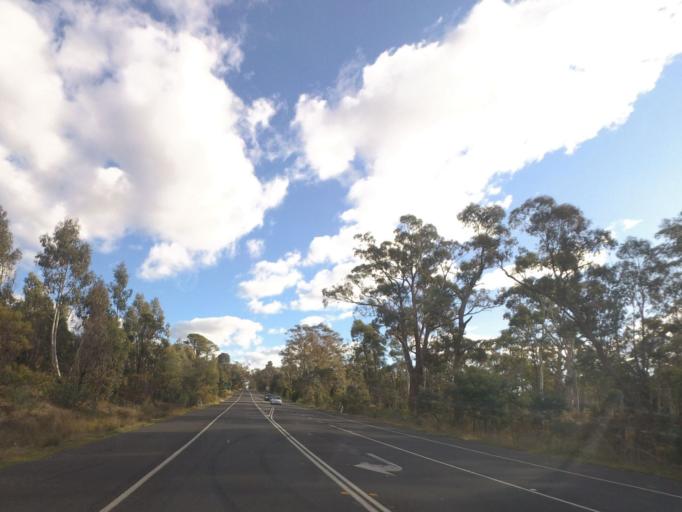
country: AU
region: Victoria
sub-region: Mount Alexander
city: Castlemaine
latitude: -37.1033
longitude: 144.3162
